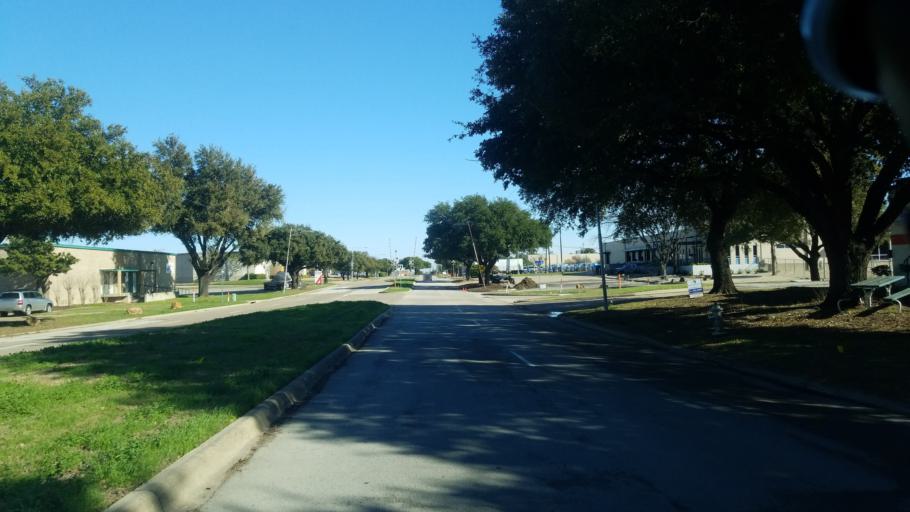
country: US
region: Texas
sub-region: Dallas County
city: Grand Prairie
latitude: 32.7565
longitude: -97.0522
